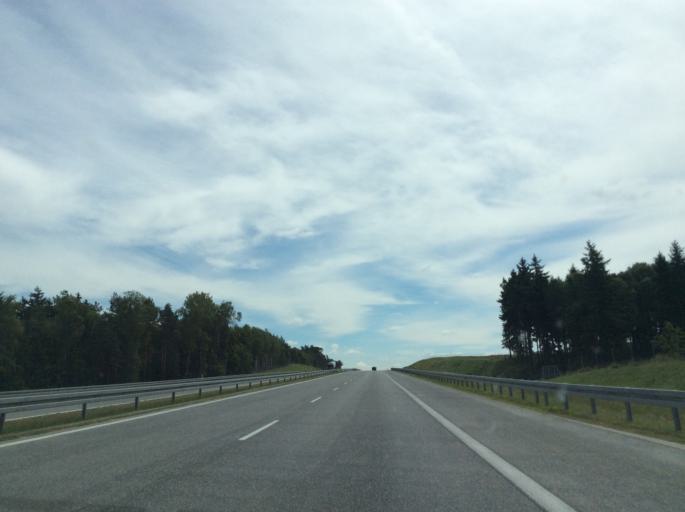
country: PL
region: Lubusz
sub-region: Powiat miedzyrzecki
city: Brojce
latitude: 52.3069
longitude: 15.6278
